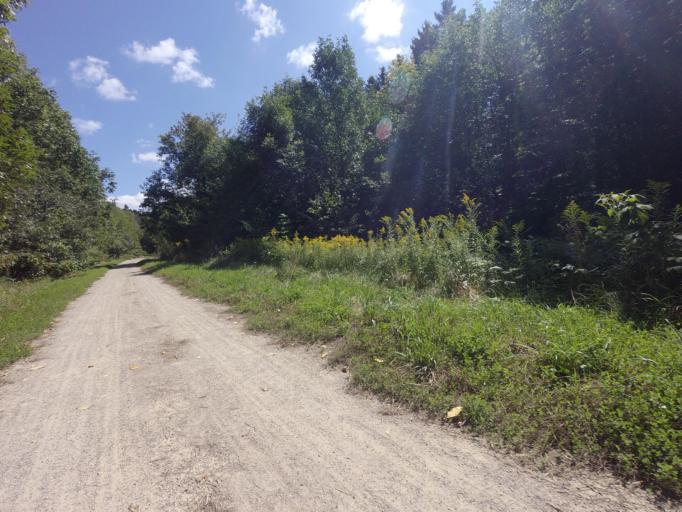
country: CA
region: Ontario
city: Orangeville
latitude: 43.7940
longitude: -80.3094
